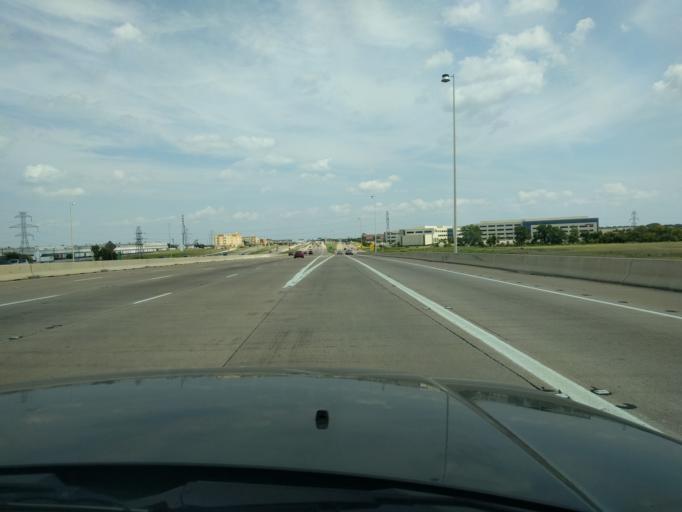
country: US
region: Texas
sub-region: Collin County
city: Plano
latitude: 33.0033
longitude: -96.6969
